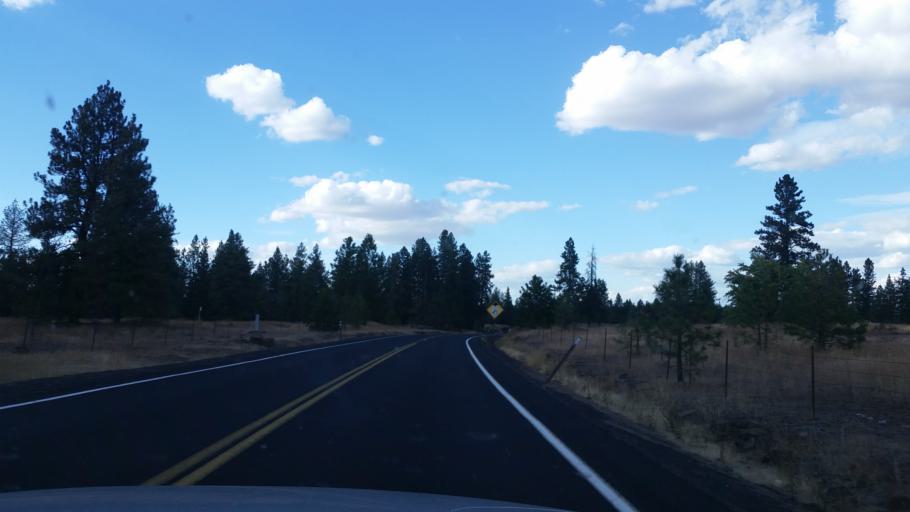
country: US
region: Washington
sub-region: Spokane County
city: Cheney
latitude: 47.4649
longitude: -117.5812
